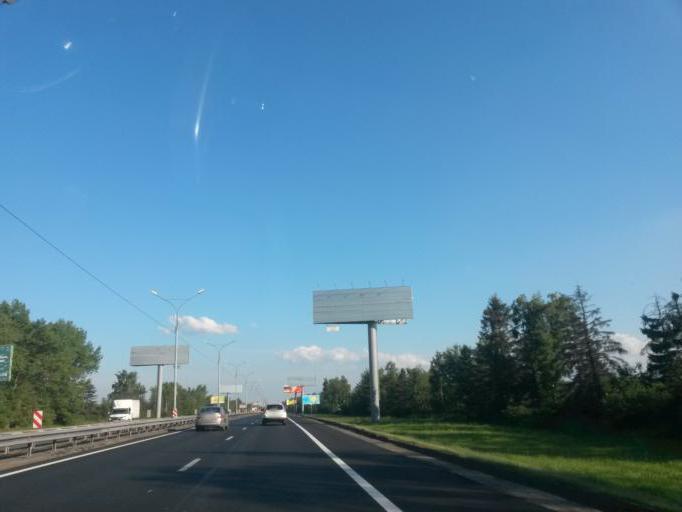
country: RU
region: Moskovskaya
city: Petrovskaya
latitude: 55.5254
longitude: 37.8187
